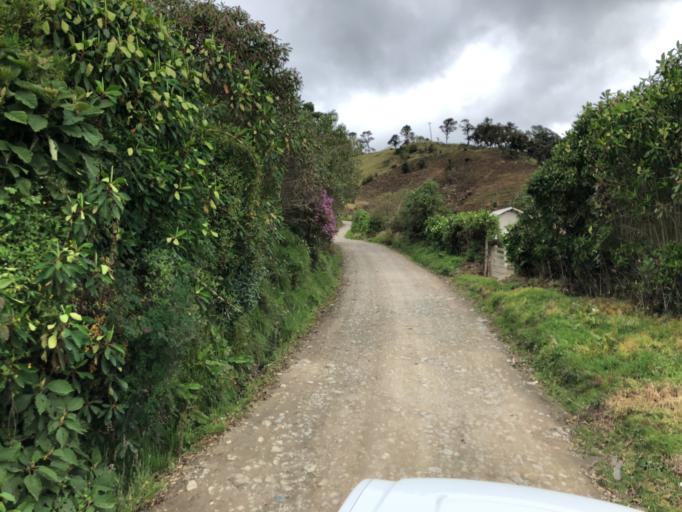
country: CO
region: Cauca
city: Totoro
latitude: 2.5023
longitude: -76.3594
